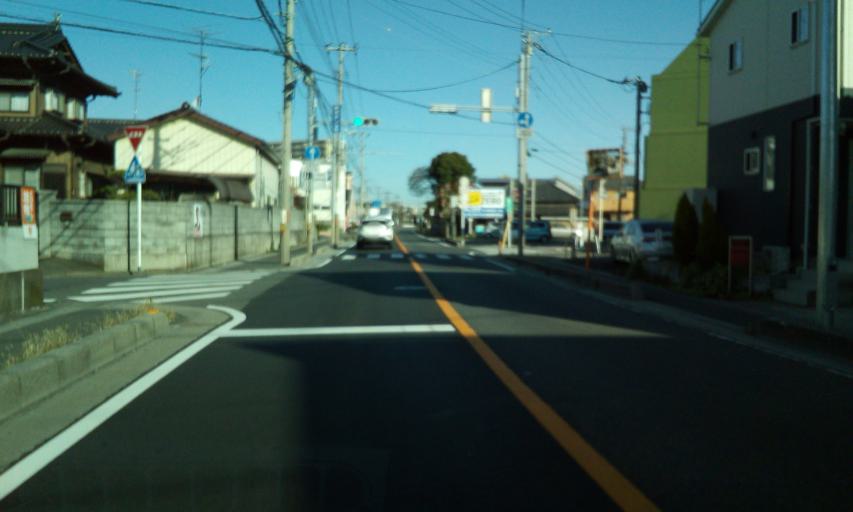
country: JP
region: Chiba
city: Nagareyama
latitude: 35.8443
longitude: 139.8810
